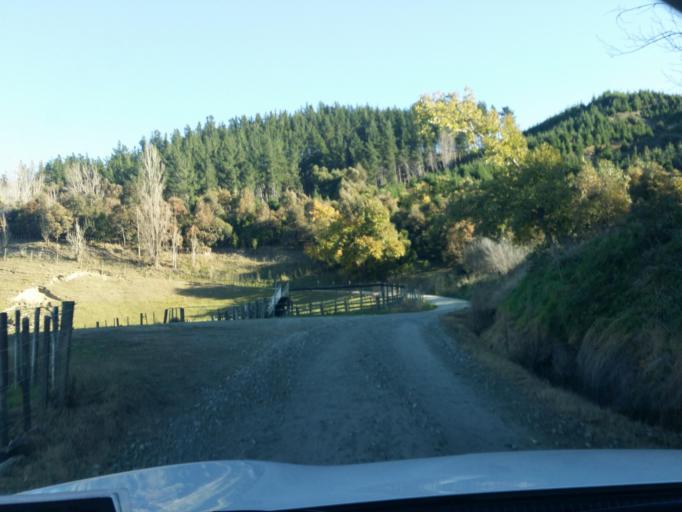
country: NZ
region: Gisborne
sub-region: Gisborne District
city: Gisborne
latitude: -38.6058
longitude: 177.8818
